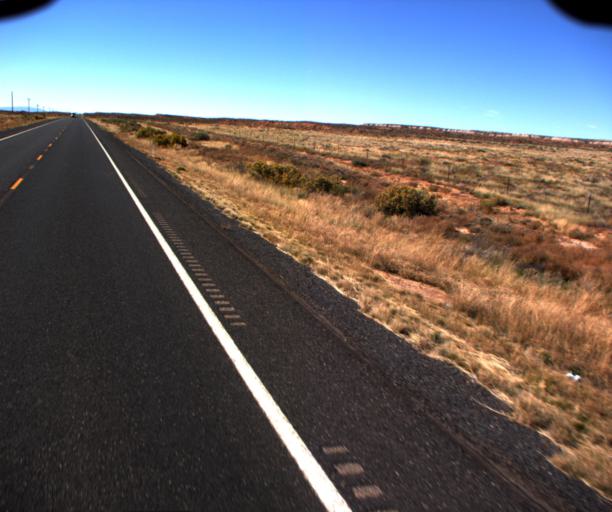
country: US
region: Arizona
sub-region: Coconino County
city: Fredonia
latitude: 36.9203
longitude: -112.5742
